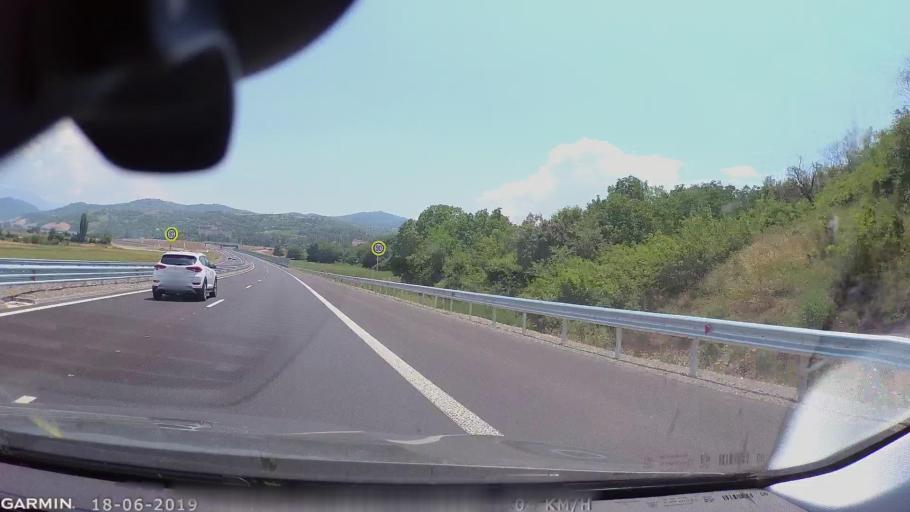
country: BG
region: Blagoevgrad
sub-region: Obshtina Blagoevgrad
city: Blagoevgrad
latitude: 41.9915
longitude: 23.0540
